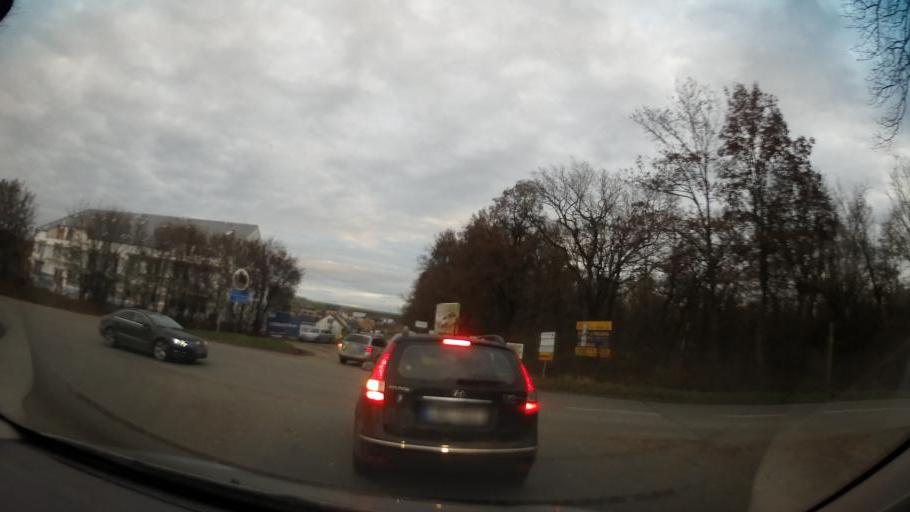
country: CZ
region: South Moravian
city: Ivancice
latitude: 49.1354
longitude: 16.3872
